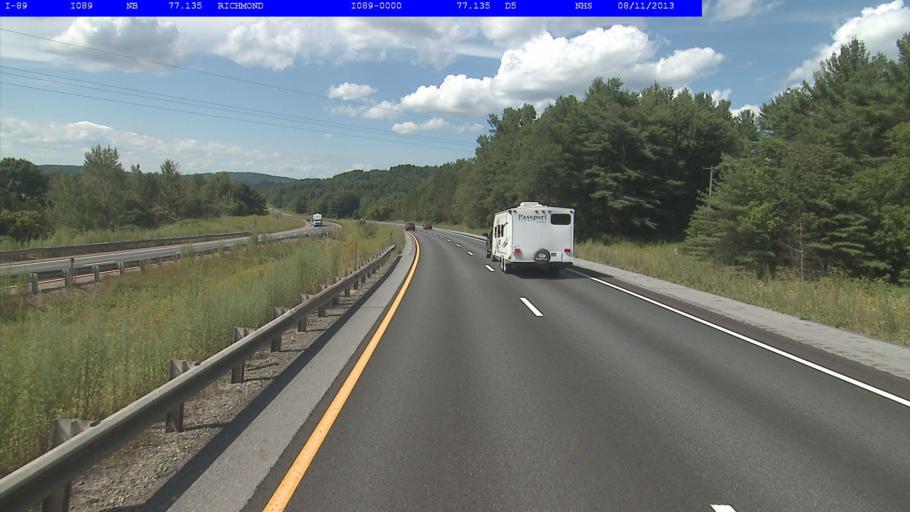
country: US
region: Vermont
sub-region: Chittenden County
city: Williston
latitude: 44.4125
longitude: -72.9916
